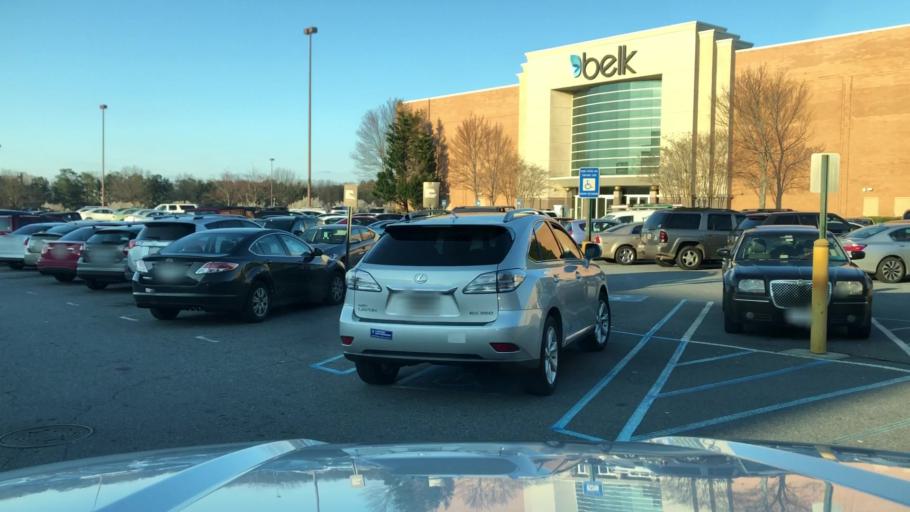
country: US
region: Georgia
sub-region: Cobb County
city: Kennesaw
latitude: 34.0185
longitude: -84.5646
